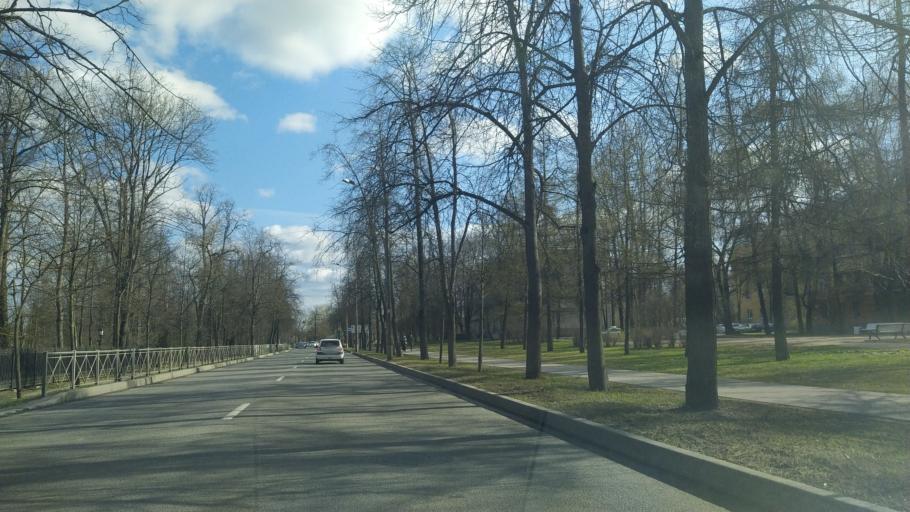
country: RU
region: St.-Petersburg
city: Pushkin
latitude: 59.7053
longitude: 30.4179
